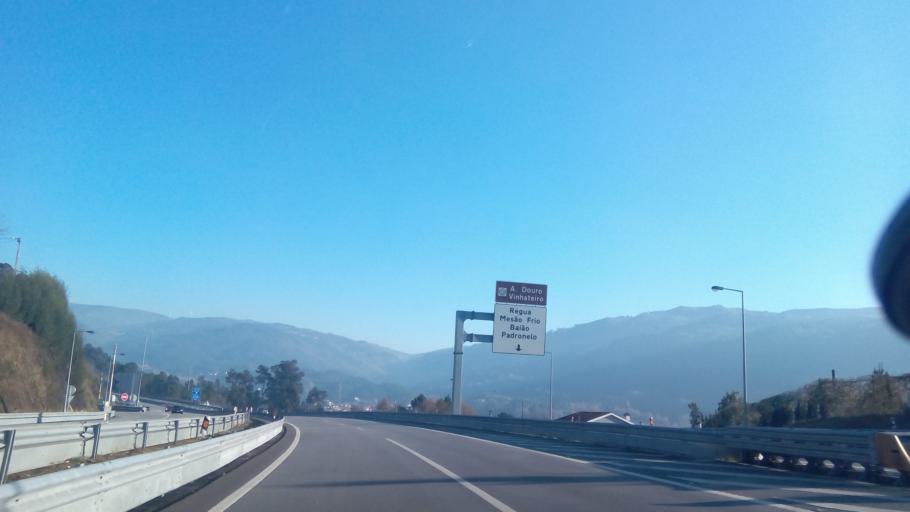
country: PT
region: Porto
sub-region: Amarante
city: Amarante
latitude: 41.2567
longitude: -8.0500
